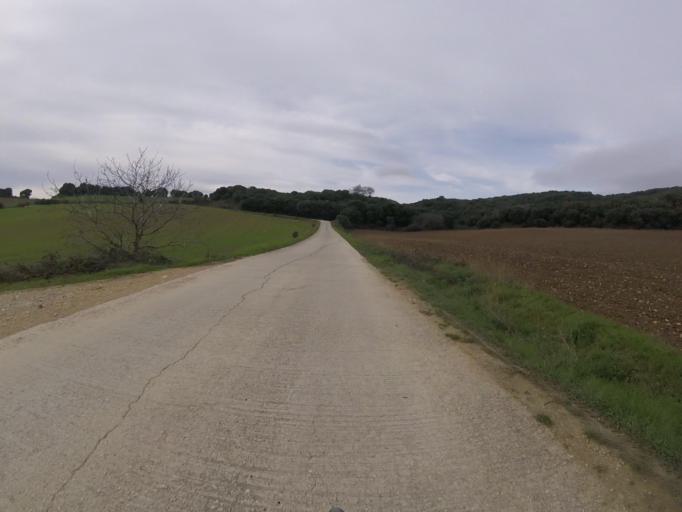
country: ES
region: Navarre
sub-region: Provincia de Navarra
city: Estella
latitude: 42.7188
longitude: -2.0417
